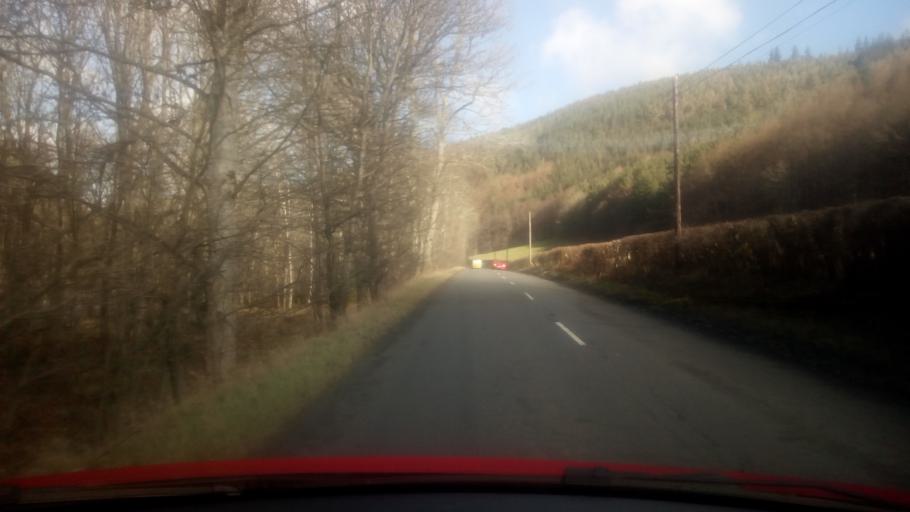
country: GB
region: Scotland
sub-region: The Scottish Borders
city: Selkirk
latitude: 55.5942
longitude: -2.8664
